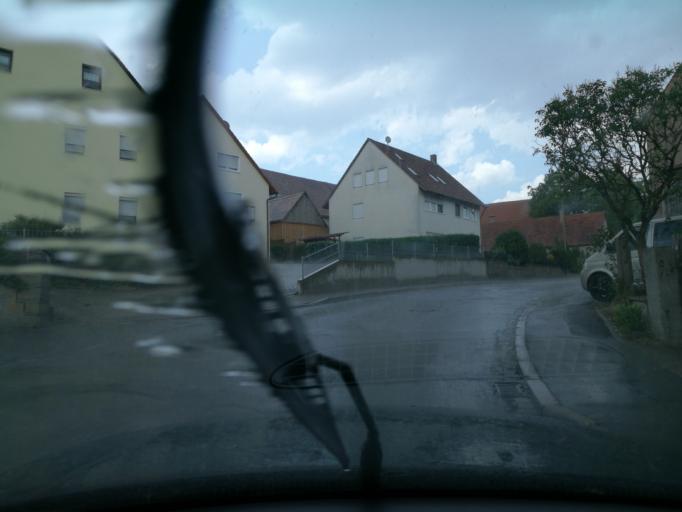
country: DE
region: Bavaria
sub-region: Regierungsbezirk Mittelfranken
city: Wilhermsdorf
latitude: 49.4437
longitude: 10.7343
